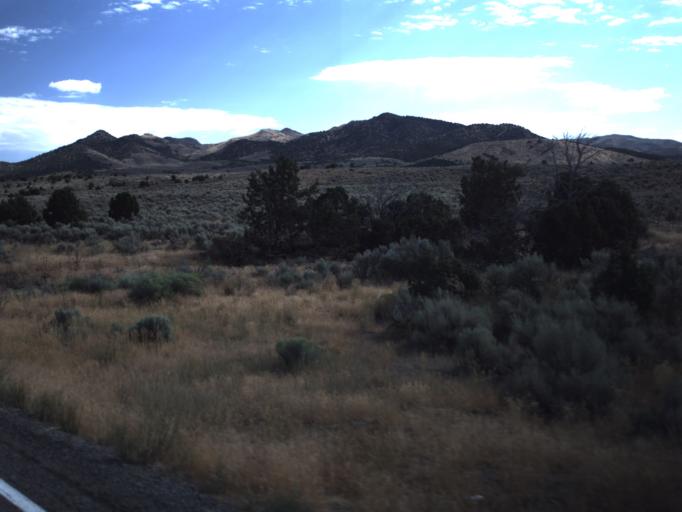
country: US
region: Utah
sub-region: Juab County
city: Mona
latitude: 39.8126
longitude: -112.1428
